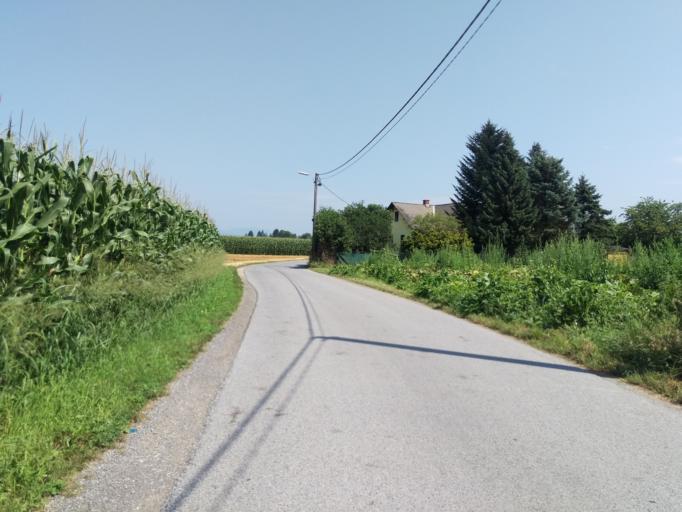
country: AT
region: Styria
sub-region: Politischer Bezirk Graz-Umgebung
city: Kalsdorf bei Graz
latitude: 46.9475
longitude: 15.4889
